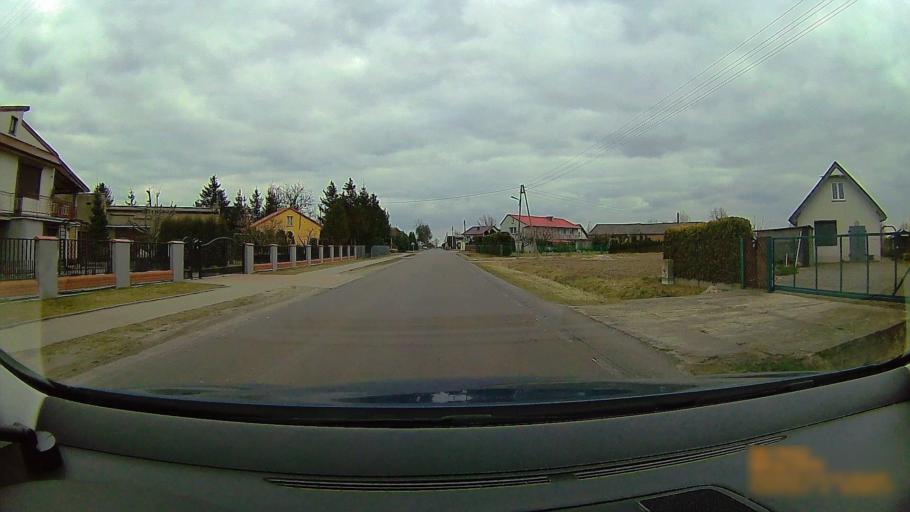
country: PL
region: Greater Poland Voivodeship
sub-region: Powiat koninski
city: Rzgow Pierwszy
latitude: 52.1235
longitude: 18.0660
